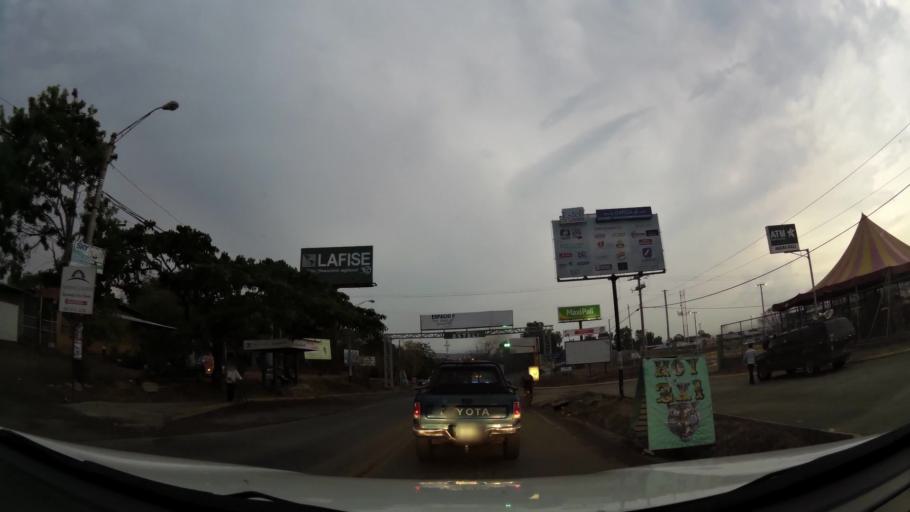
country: NI
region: Esteli
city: Esteli
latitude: 13.0709
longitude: -86.3513
